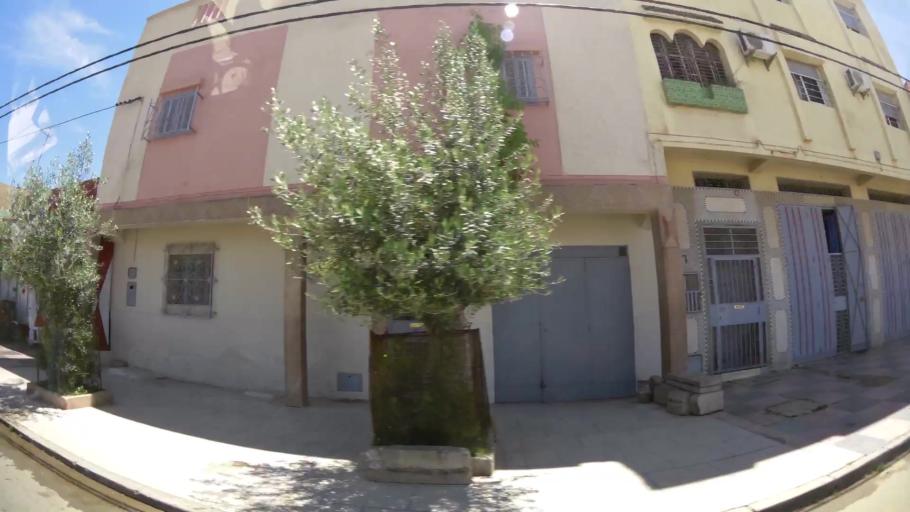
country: MA
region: Oriental
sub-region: Oujda-Angad
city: Oujda
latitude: 34.6725
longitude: -1.9309
